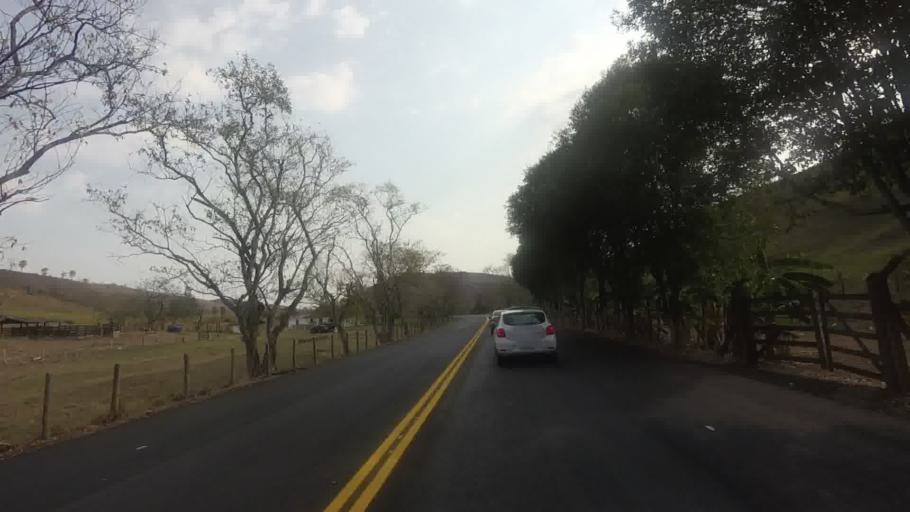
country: BR
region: Rio de Janeiro
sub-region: Bom Jesus Do Itabapoana
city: Bom Jesus do Itabapoana
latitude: -21.2229
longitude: -41.7413
